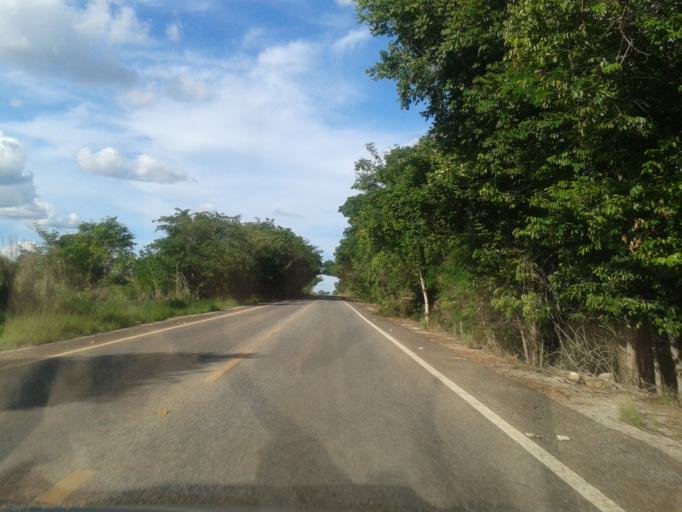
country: BR
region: Goias
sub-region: Mozarlandia
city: Mozarlandia
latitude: -14.4809
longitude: -50.4765
